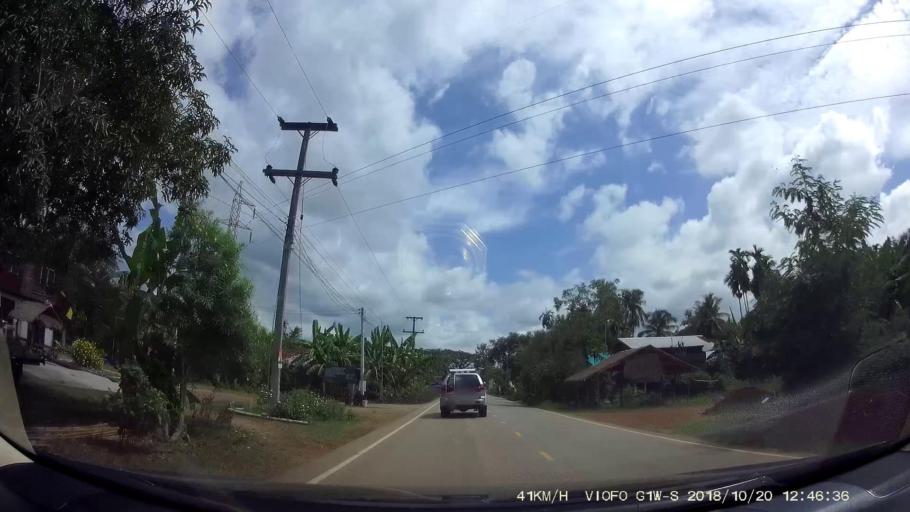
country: TH
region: Chaiyaphum
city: Khon San
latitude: 16.5331
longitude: 101.8813
